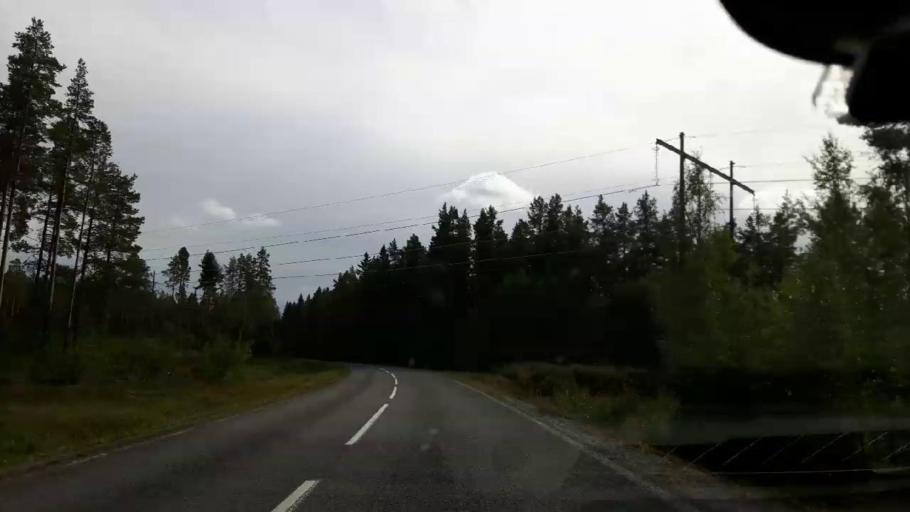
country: SE
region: Jaemtland
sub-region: Ragunda Kommun
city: Hammarstrand
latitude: 63.1396
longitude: 15.8634
